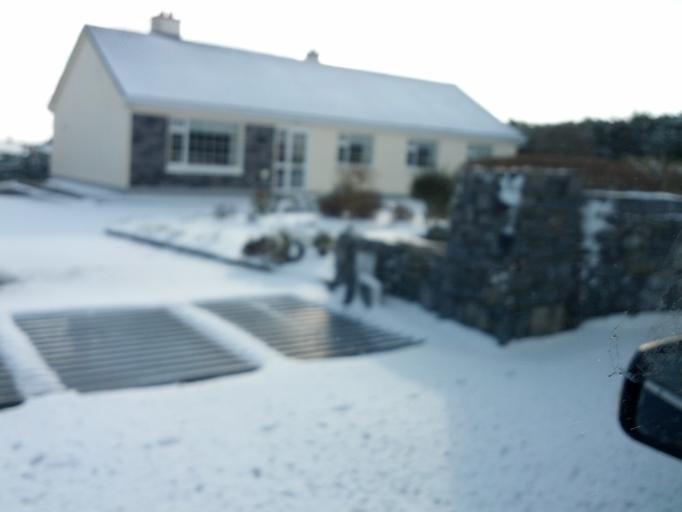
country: IE
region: Connaught
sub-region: County Galway
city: Athenry
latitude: 53.2042
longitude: -8.7757
